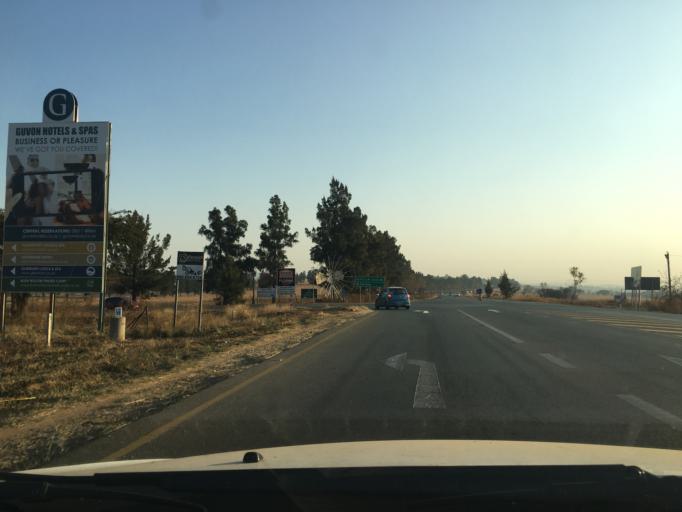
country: ZA
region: Gauteng
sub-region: West Rand District Municipality
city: Muldersdriseloop
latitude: -25.9949
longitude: 27.8574
